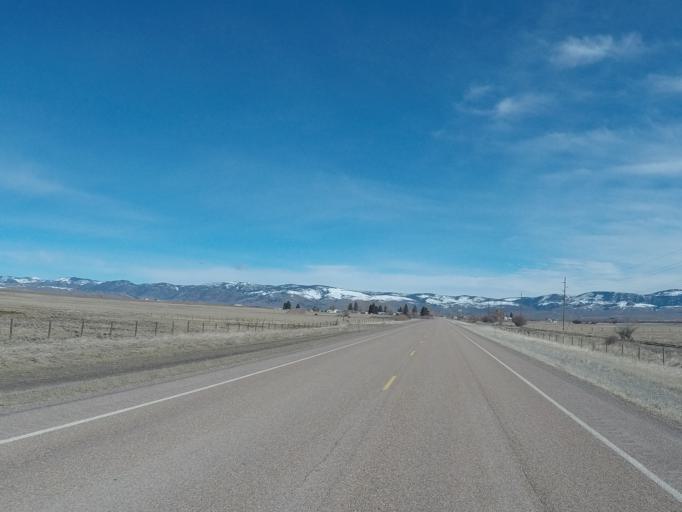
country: US
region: Montana
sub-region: Granite County
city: Philipsburg
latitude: 46.5764
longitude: -113.2027
